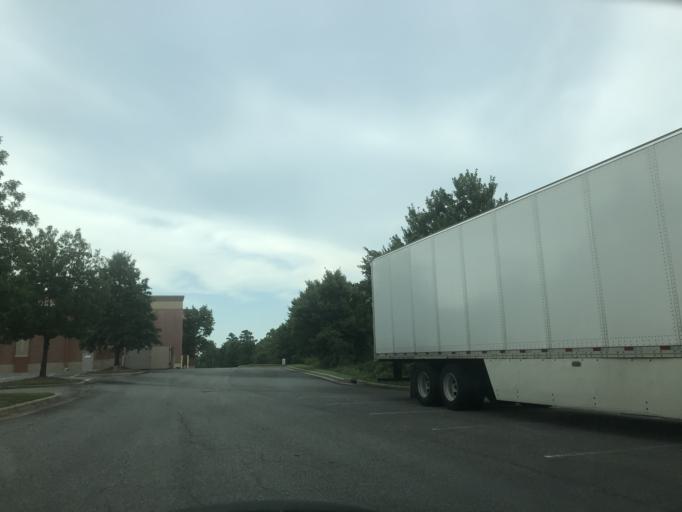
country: US
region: North Carolina
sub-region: Wake County
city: Morrisville
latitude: 35.9030
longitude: -78.7844
